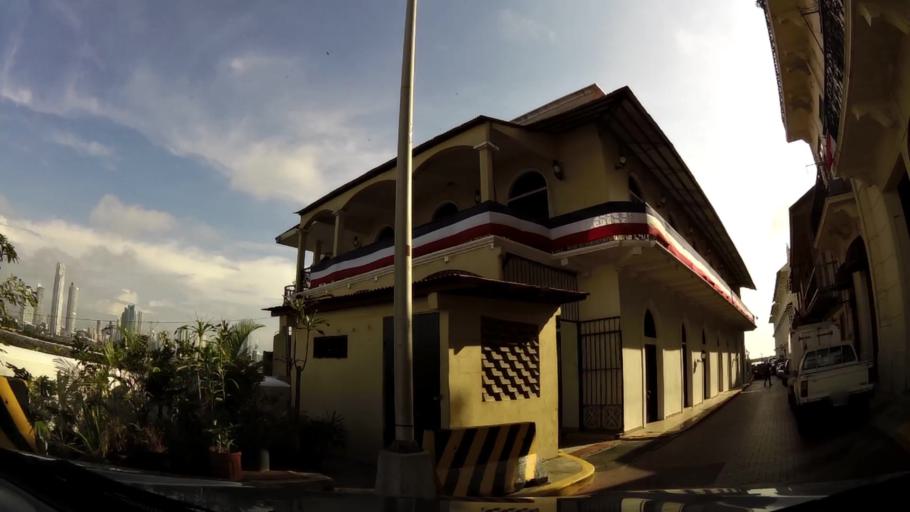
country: PA
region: Panama
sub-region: Distrito de Panama
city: Ancon
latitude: 8.9541
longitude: -79.5336
